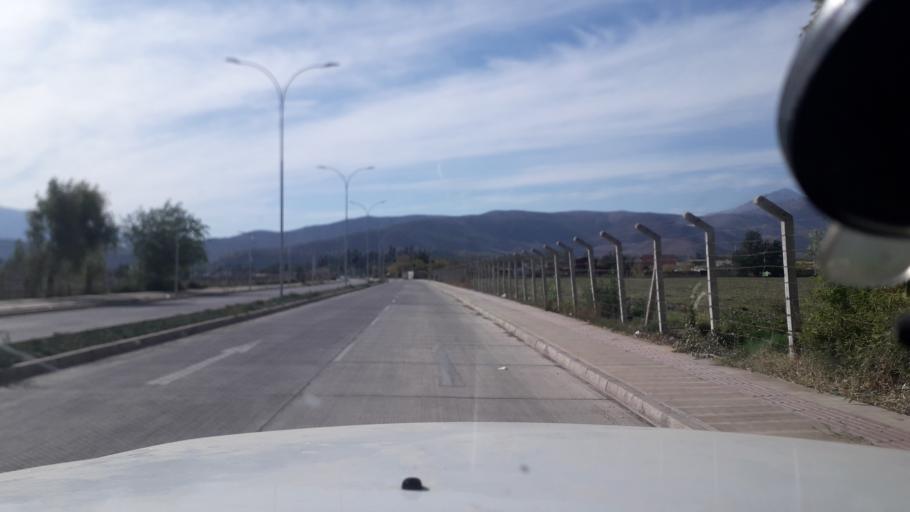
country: CL
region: Valparaiso
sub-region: Provincia de San Felipe
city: San Felipe
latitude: -32.7475
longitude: -70.7106
